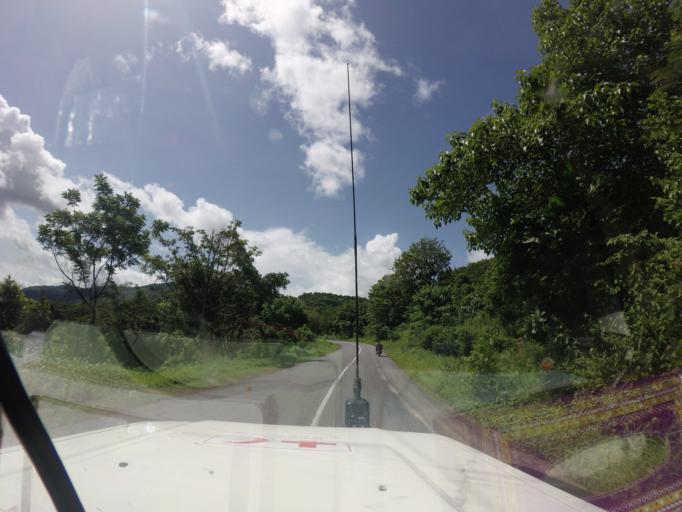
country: GN
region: Mamou
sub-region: Mamou Prefecture
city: Mamou
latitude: 10.2147
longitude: -11.8546
